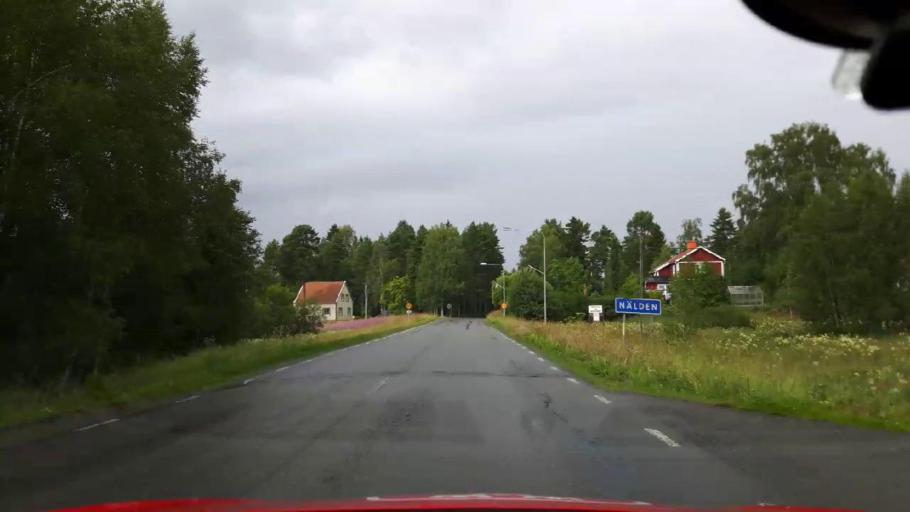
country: SE
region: Jaemtland
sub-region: Krokoms Kommun
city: Krokom
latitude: 63.3458
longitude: 14.2614
